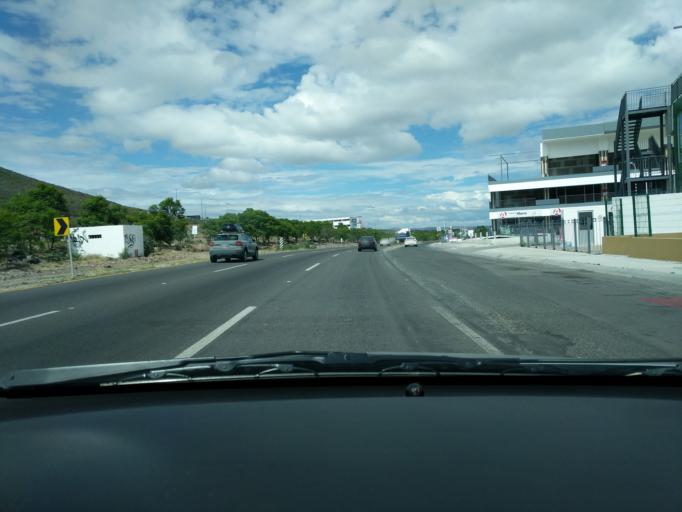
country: MX
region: Queretaro
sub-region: El Marques
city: La Pradera
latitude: 20.6610
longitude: -100.3493
